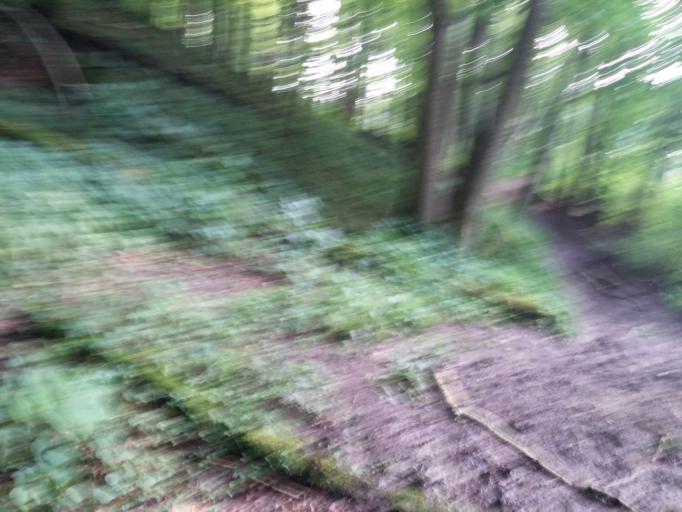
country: DE
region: Bavaria
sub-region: Swabia
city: Kronburg
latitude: 47.8655
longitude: 10.1908
